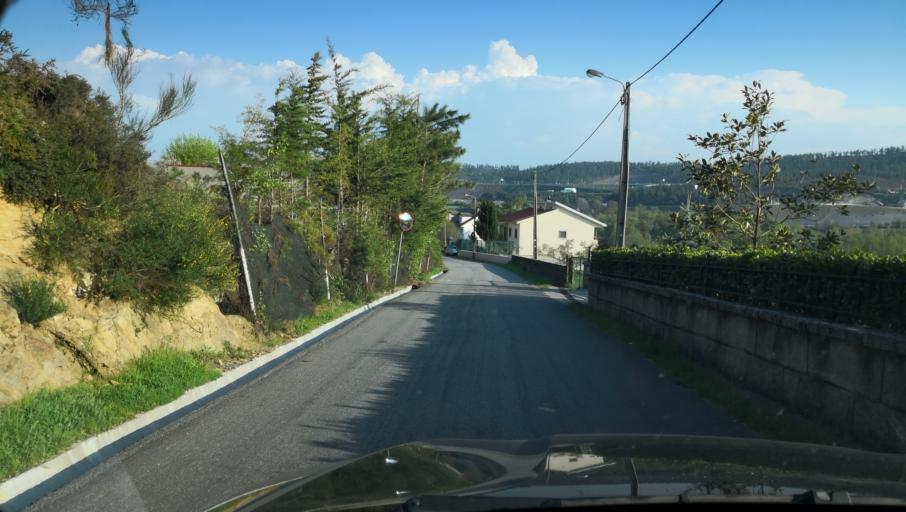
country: PT
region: Vila Real
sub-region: Santa Marta de Penaguiao
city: Santa Marta de Penaguiao
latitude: 41.2901
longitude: -7.8359
